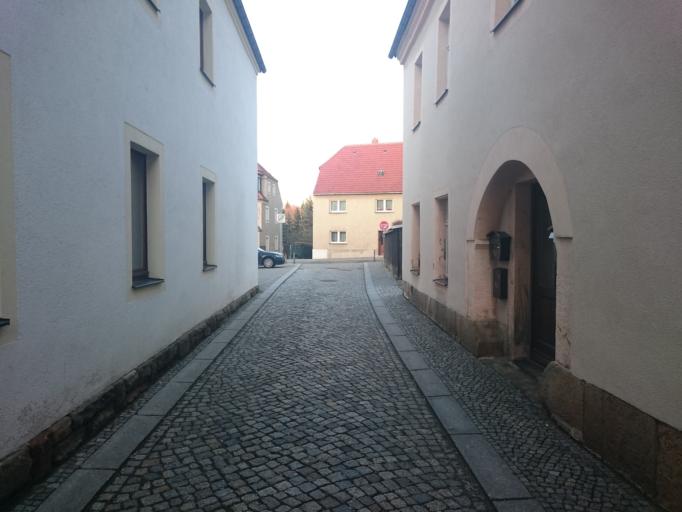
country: DE
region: Saxony
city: Dippoldiswalde
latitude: 50.8967
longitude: 13.6696
